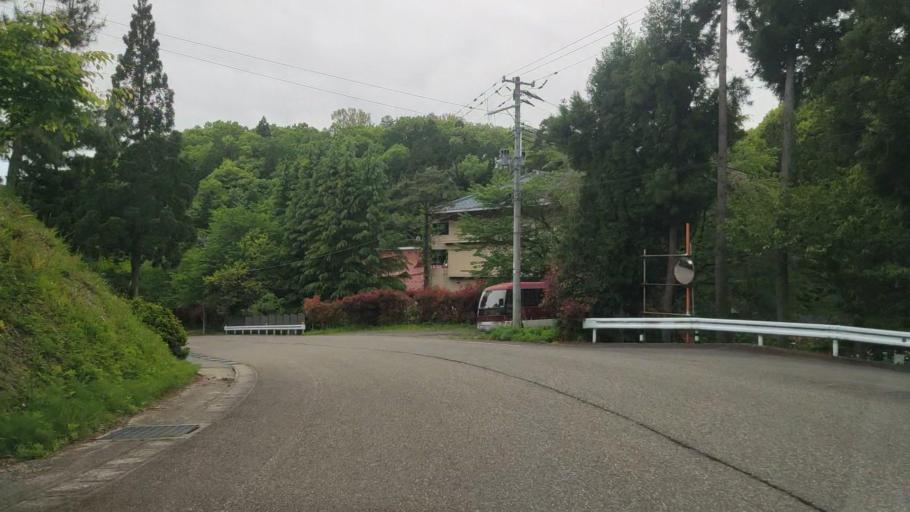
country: JP
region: Niigata
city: Kamo
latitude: 37.7158
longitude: 139.0830
